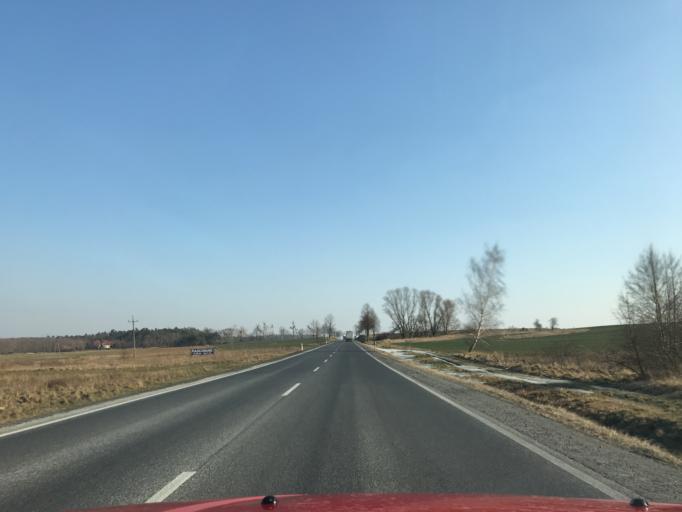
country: PL
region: Greater Poland Voivodeship
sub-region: Powiat sredzki
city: Nowe Miasto nad Warta
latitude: 52.0825
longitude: 17.4055
